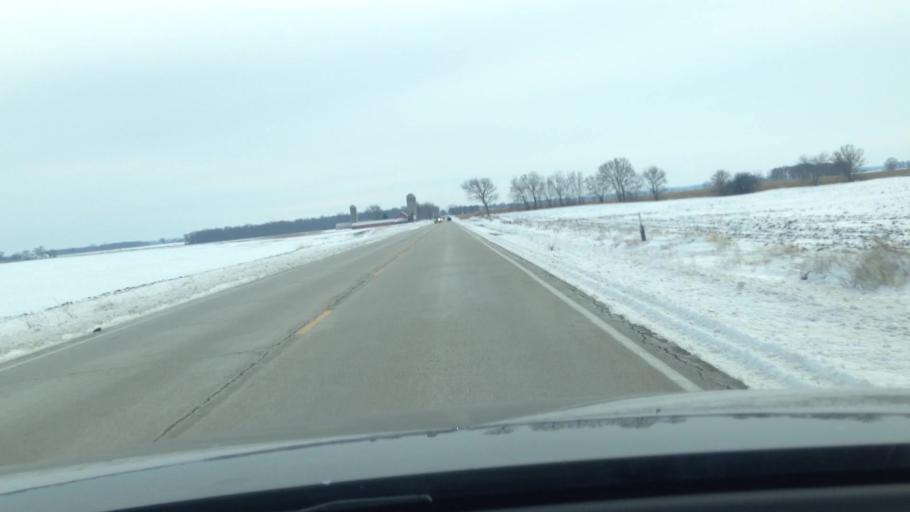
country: US
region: Illinois
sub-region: McHenry County
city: Hebron
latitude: 42.4351
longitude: -88.4381
